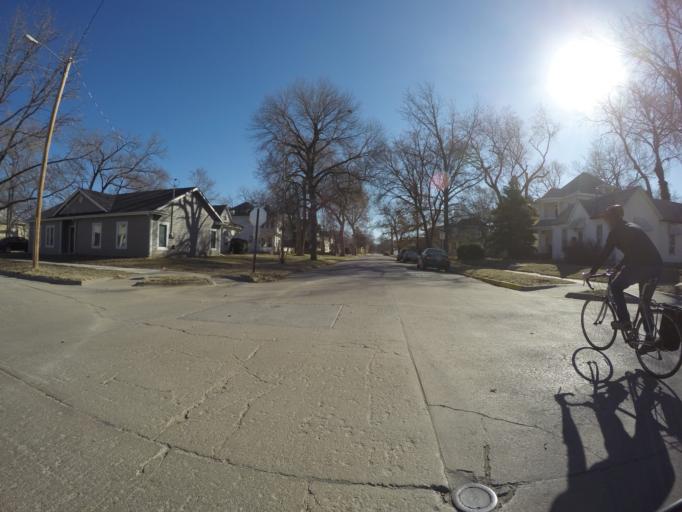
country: US
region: Kansas
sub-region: Riley County
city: Manhattan
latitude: 39.1784
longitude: -96.5734
